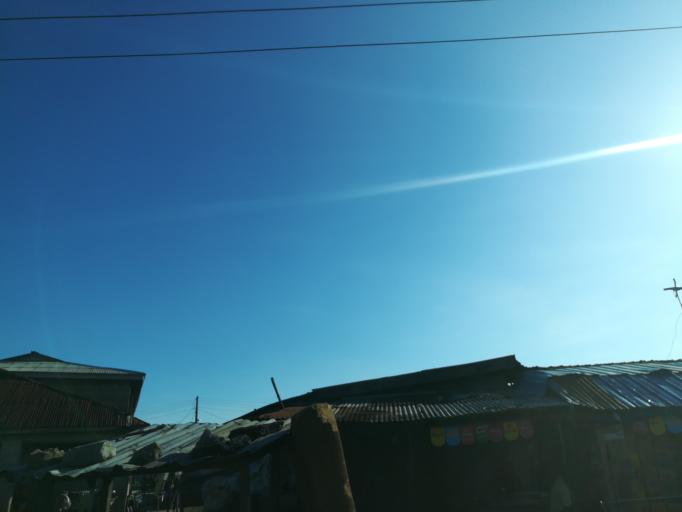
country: NG
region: Lagos
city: Ikorodu
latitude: 6.5384
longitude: 3.5516
